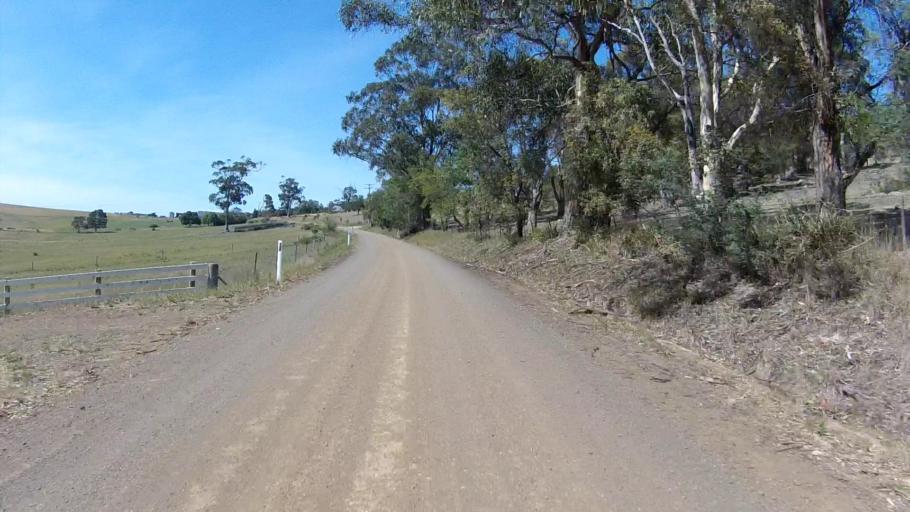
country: AU
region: Tasmania
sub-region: Sorell
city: Sorell
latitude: -42.7384
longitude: 147.5982
